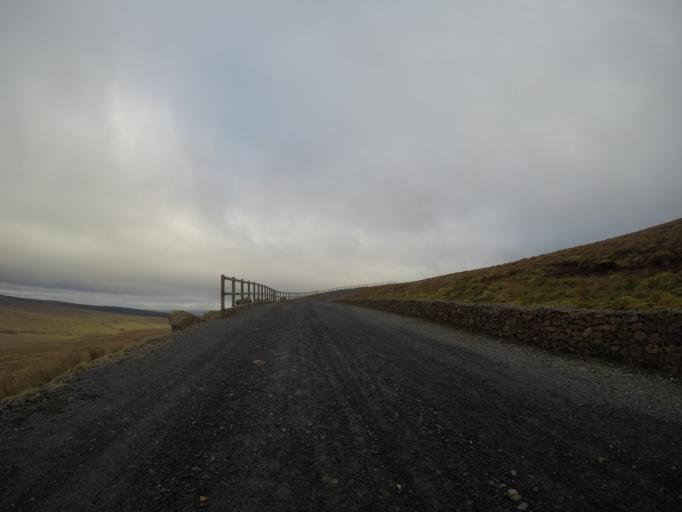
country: GB
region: Scotland
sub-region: North Ayrshire
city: Fairlie
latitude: 55.7634
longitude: -4.7939
